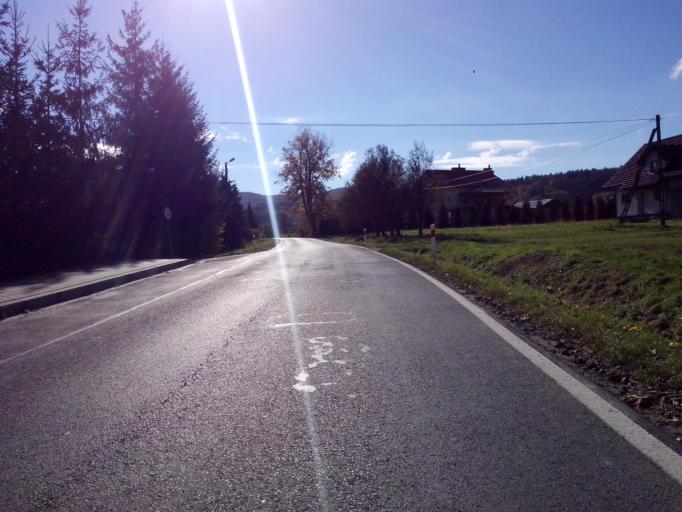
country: PL
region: Subcarpathian Voivodeship
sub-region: Powiat krosnienski
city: Korczyna
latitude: 49.7761
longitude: 21.8527
